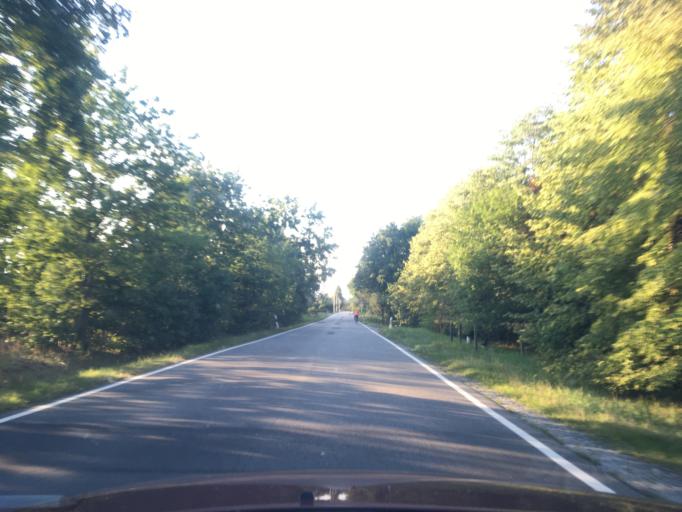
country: DE
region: Saxony
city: Rothenburg
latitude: 51.3248
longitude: 14.9746
